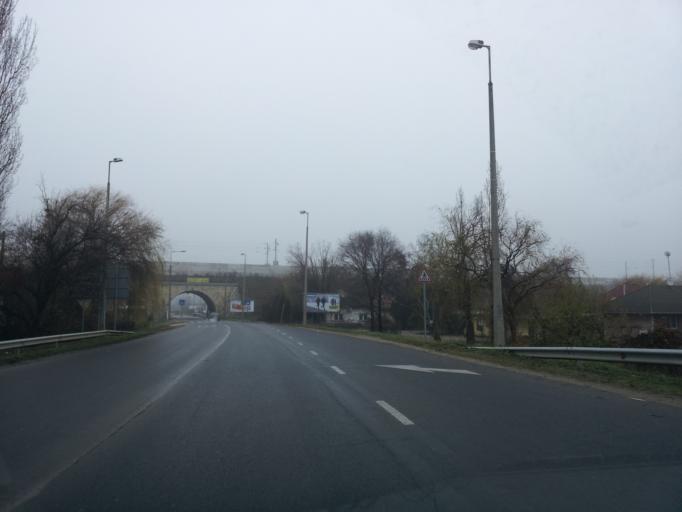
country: HU
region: Pest
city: Erd
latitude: 47.3806
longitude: 18.9367
